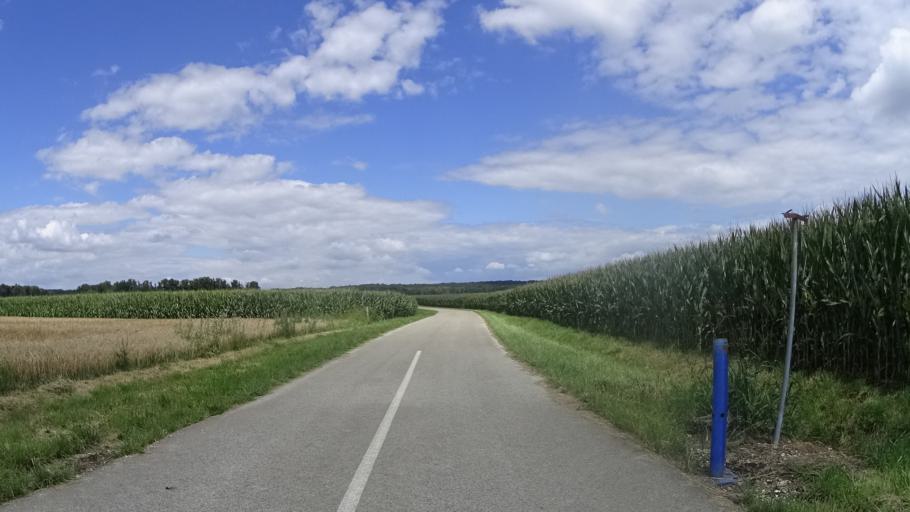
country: FR
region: Champagne-Ardenne
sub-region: Departement de la Haute-Marne
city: Montier-en-Der
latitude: 48.5123
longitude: 4.7746
